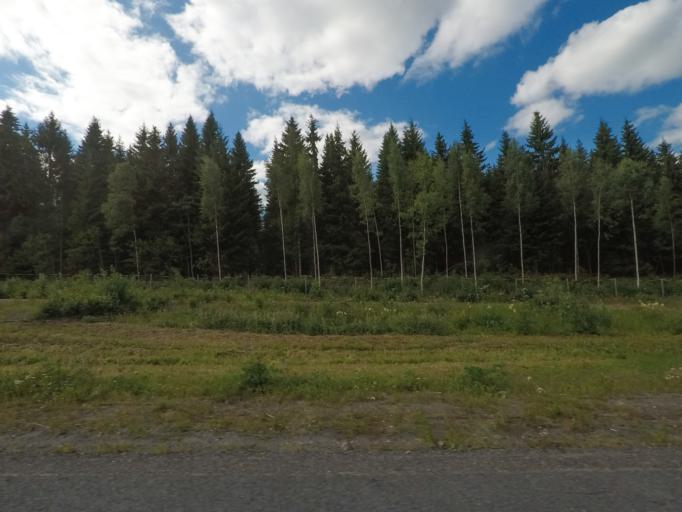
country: FI
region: Southern Savonia
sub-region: Mikkeli
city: Maentyharju
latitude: 61.4511
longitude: 26.7023
